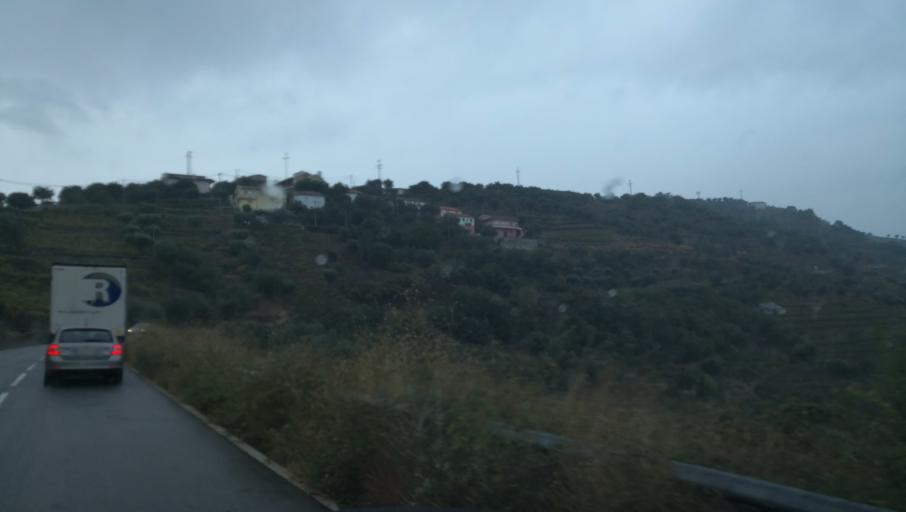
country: PT
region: Vila Real
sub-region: Santa Marta de Penaguiao
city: Santa Marta de Penaguiao
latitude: 41.2250
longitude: -7.7257
